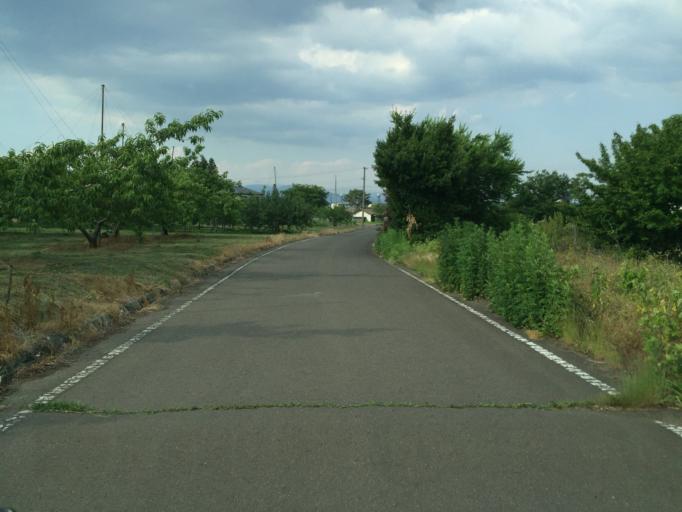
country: JP
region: Fukushima
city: Fukushima-shi
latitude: 37.7078
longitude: 140.3739
